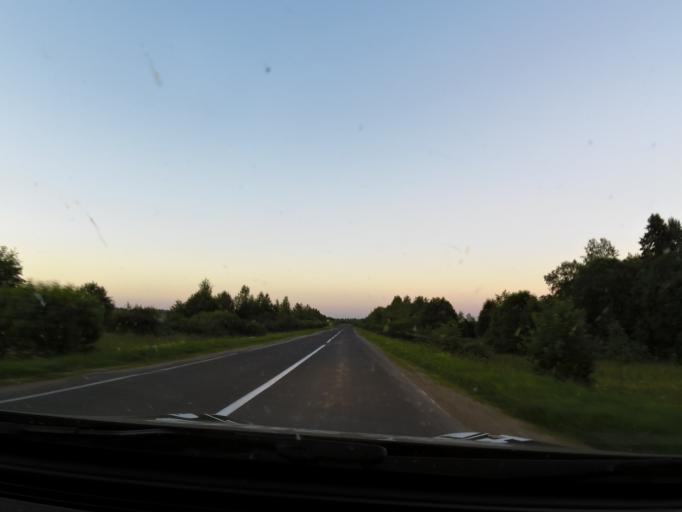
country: RU
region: Jaroslavl
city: Lyubim
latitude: 58.3387
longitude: 41.0888
